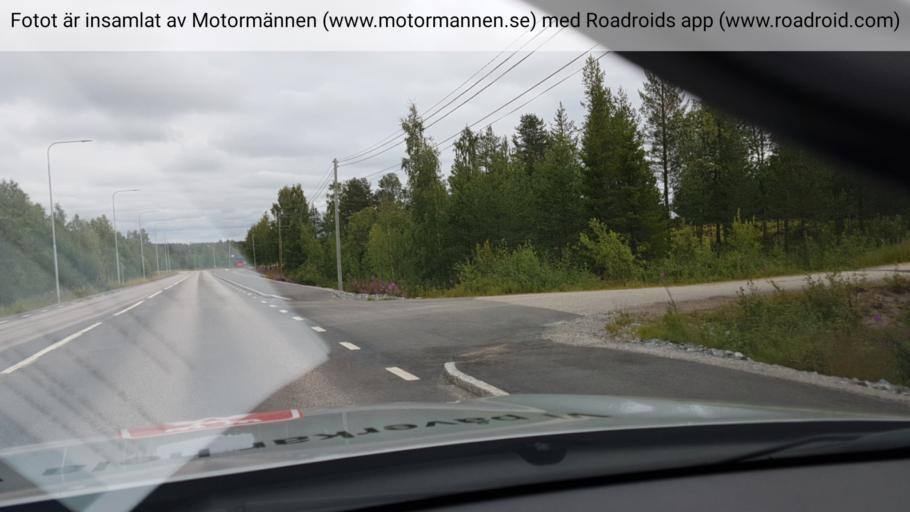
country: SE
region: Norrbotten
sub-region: Gallivare Kommun
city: Gaellivare
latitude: 67.0662
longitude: 21.2896
